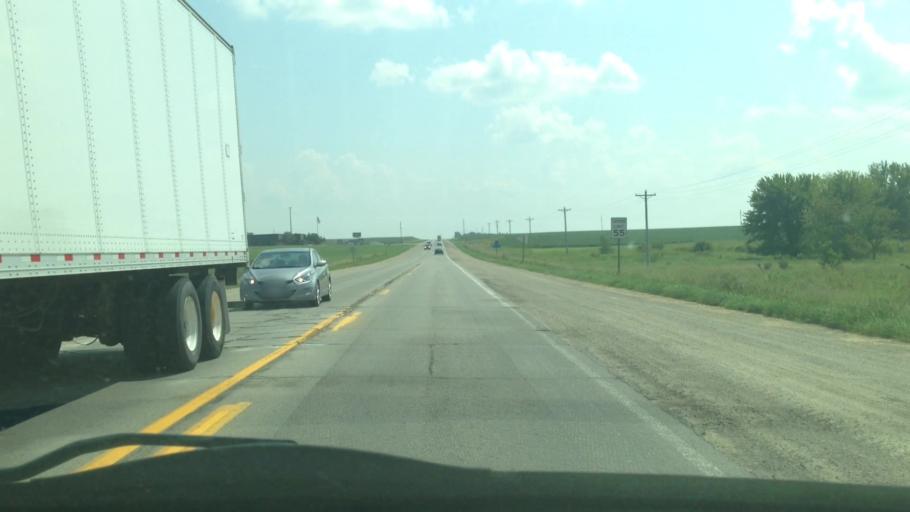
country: US
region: Iowa
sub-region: Howard County
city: Cresco
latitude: 43.3701
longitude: -92.2983
